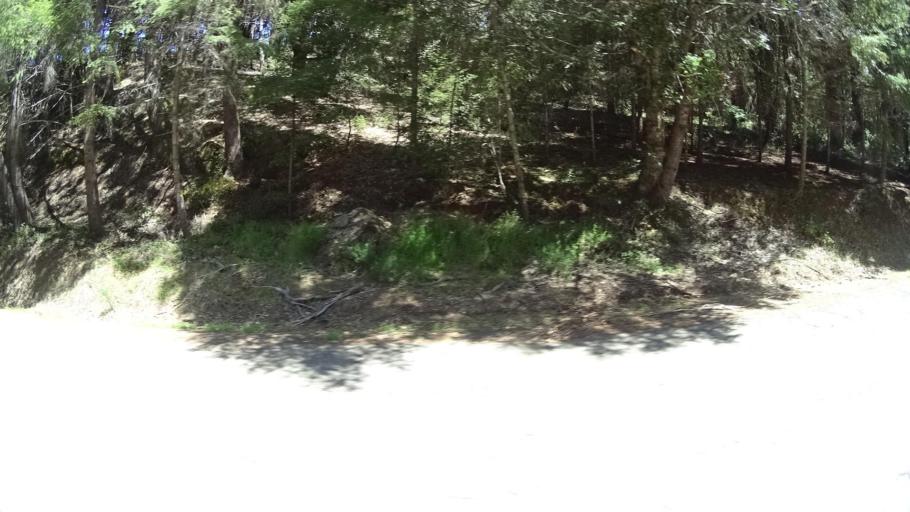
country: US
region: California
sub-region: Humboldt County
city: Redway
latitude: 40.1135
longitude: -123.9638
